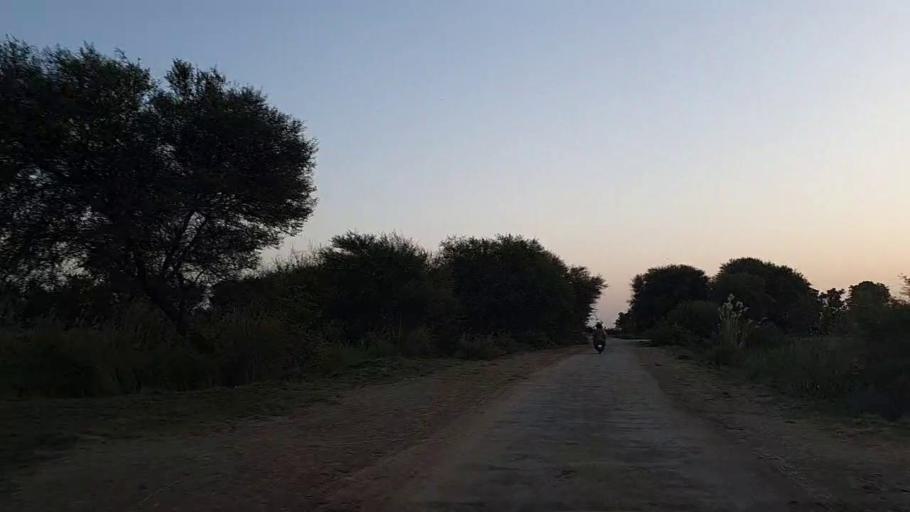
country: PK
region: Sindh
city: Mirpur Batoro
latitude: 24.6176
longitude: 68.1838
